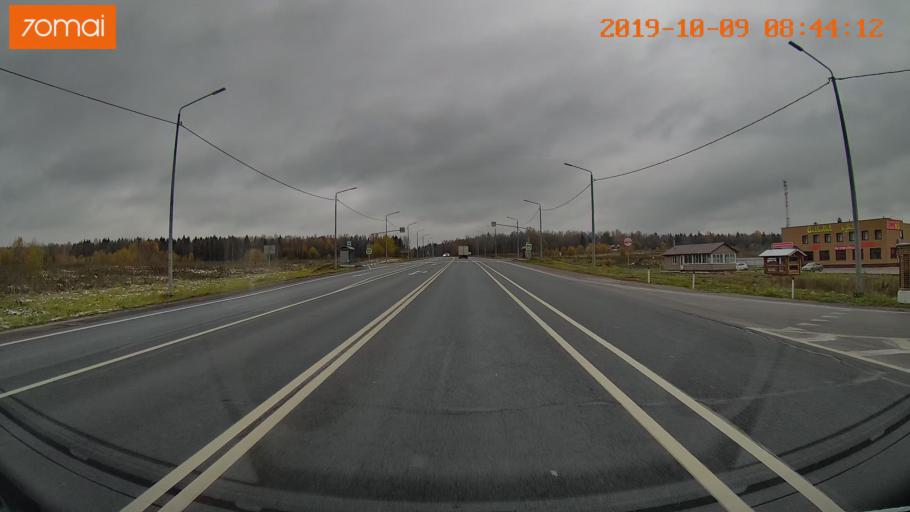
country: RU
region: Vologda
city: Gryazovets
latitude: 59.0332
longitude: 40.1099
